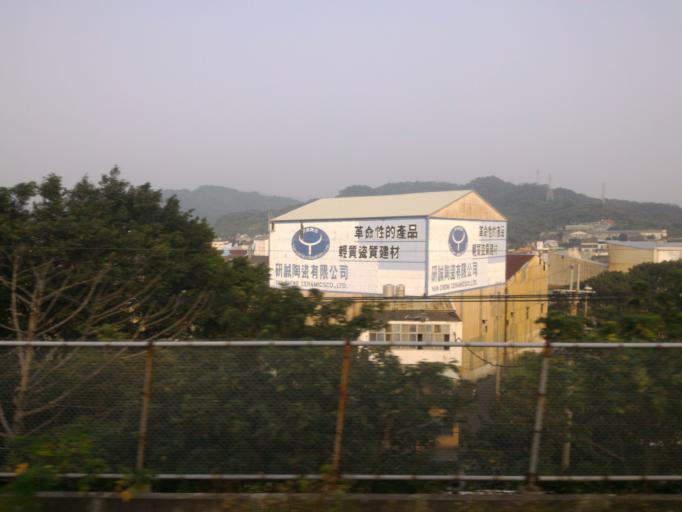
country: TW
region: Taiwan
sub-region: Taoyuan
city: Taoyuan
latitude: 24.9619
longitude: 121.3384
